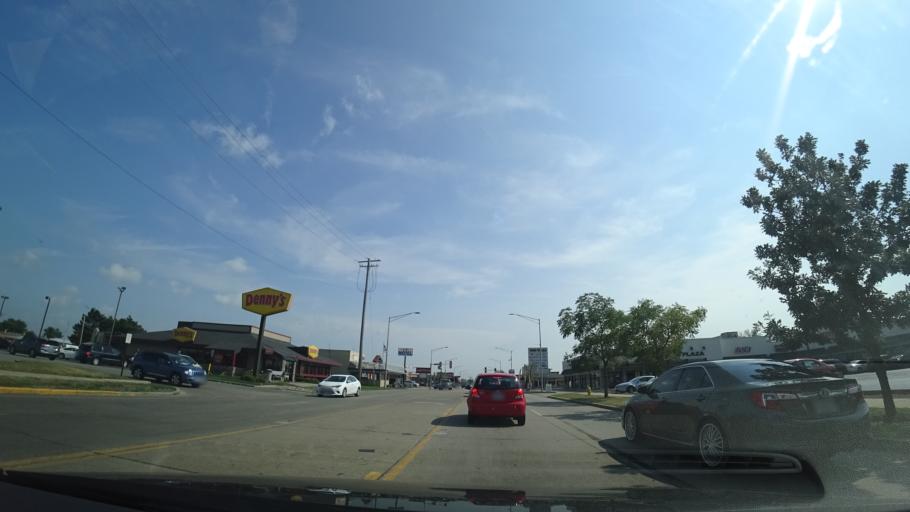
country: US
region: Illinois
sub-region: Cook County
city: Harwood Heights
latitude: 41.9648
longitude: -87.8073
